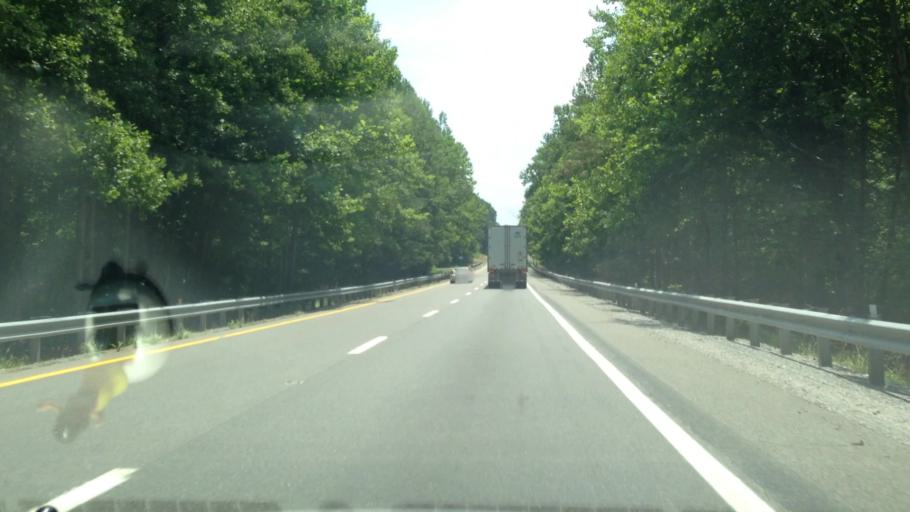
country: US
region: Virginia
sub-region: City of Martinsville
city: Martinsville
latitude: 36.6344
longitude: -79.8887
